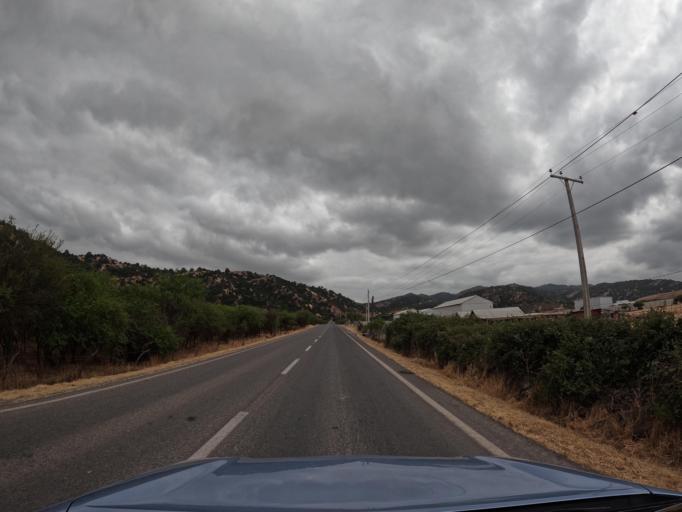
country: CL
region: Maule
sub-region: Provincia de Curico
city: Teno
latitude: -34.8292
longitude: -71.1907
